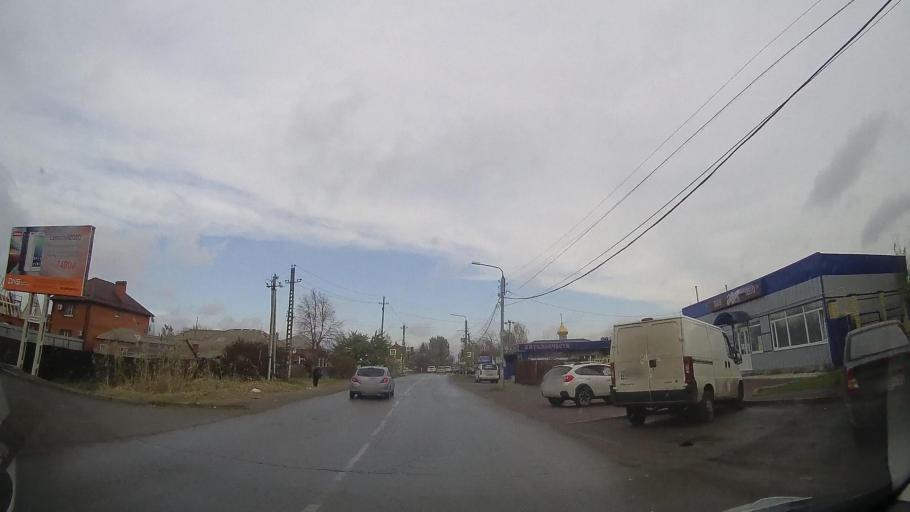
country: RU
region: Rostov
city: Bataysk
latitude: 47.1379
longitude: 39.7676
